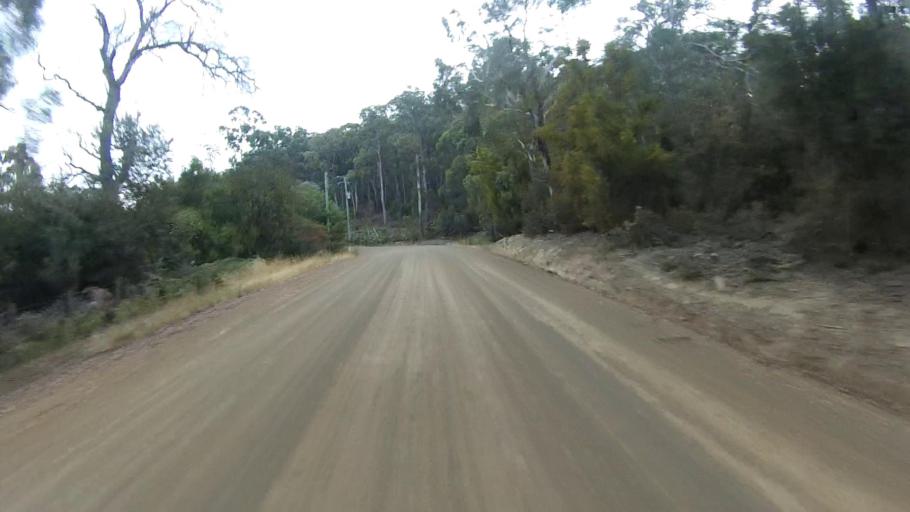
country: AU
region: Tasmania
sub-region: Huon Valley
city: Cygnet
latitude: -43.2240
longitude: 147.0937
